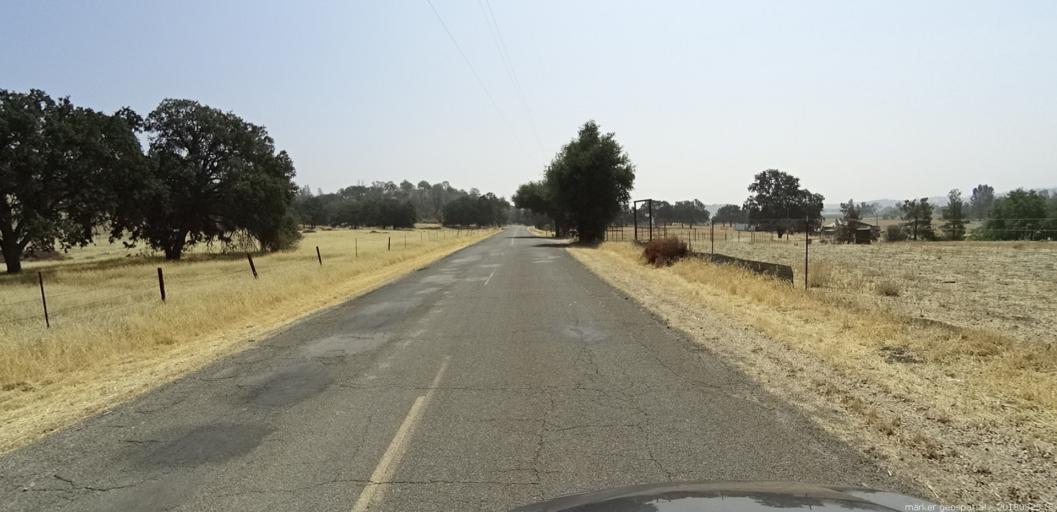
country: US
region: California
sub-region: Fresno County
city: Coalinga
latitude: 35.9054
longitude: -120.4560
